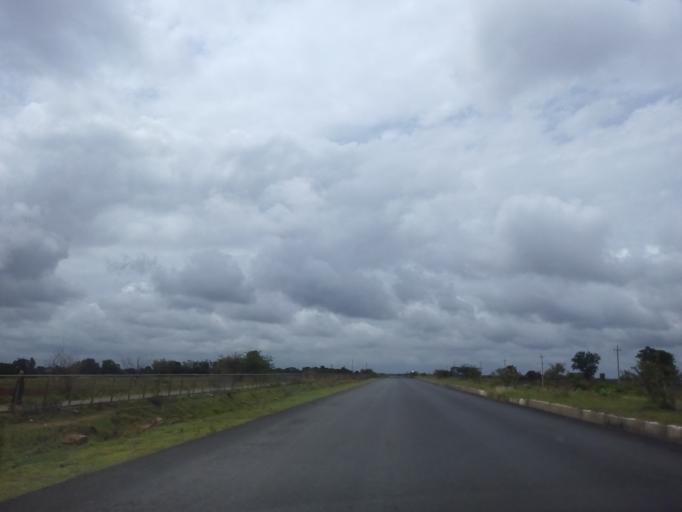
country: IN
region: Karnataka
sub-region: Haveri
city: Byadgi
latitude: 14.6900
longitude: 75.5339
